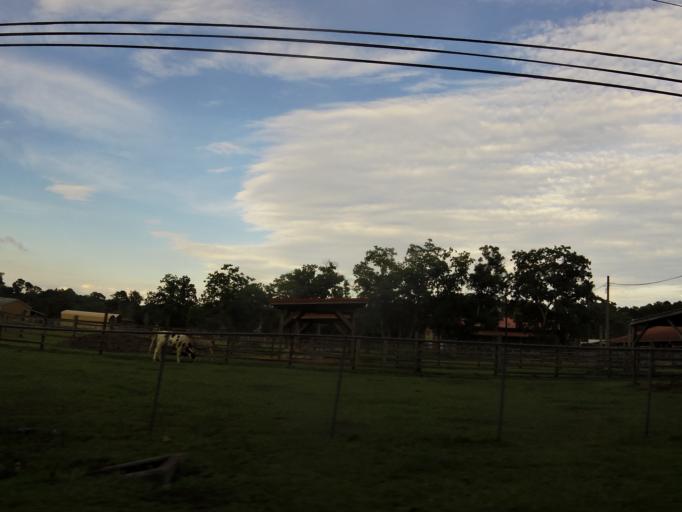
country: US
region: Florida
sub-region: Duval County
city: Jacksonville
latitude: 30.3227
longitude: -81.8066
